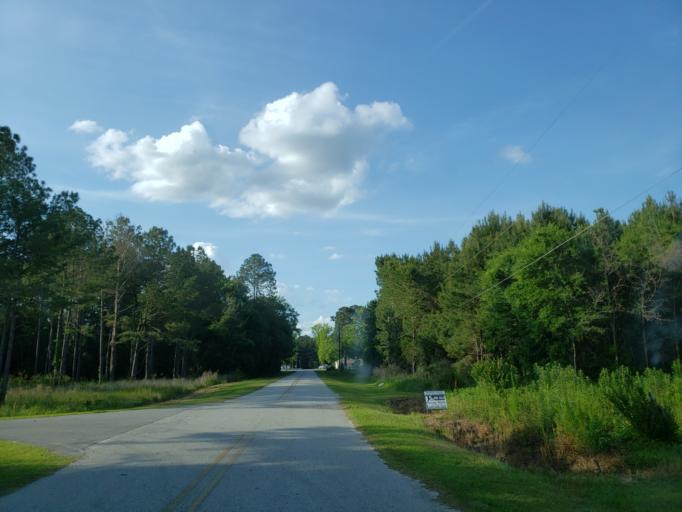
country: US
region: Georgia
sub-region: Lowndes County
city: Hahira
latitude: 31.0449
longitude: -83.3873
